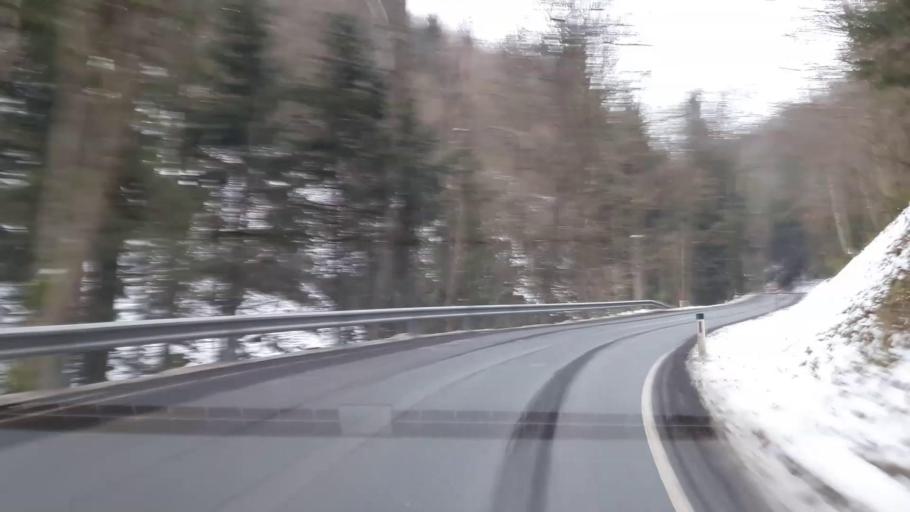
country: AT
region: Lower Austria
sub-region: Politischer Bezirk Neunkirchen
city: Feistritz am Wechsel
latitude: 47.5543
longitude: 16.0799
